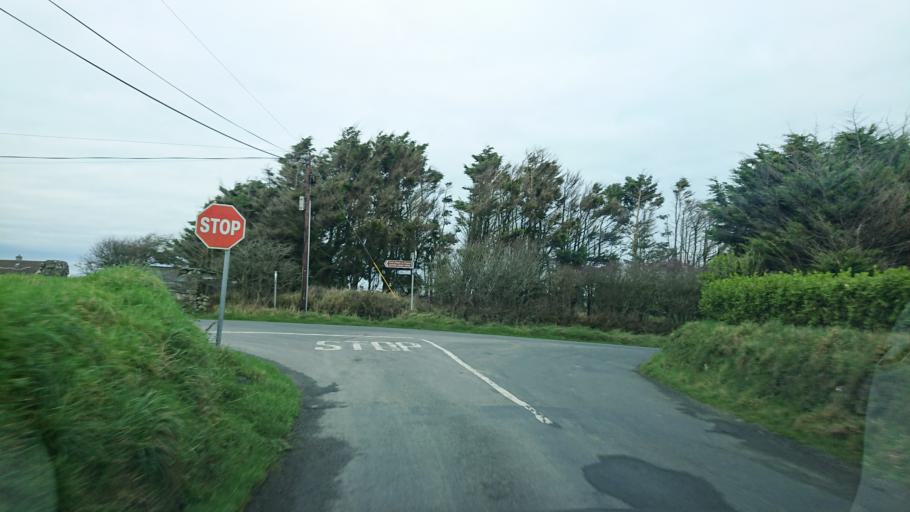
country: IE
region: Munster
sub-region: Waterford
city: Tra Mhor
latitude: 52.1456
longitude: -7.1806
